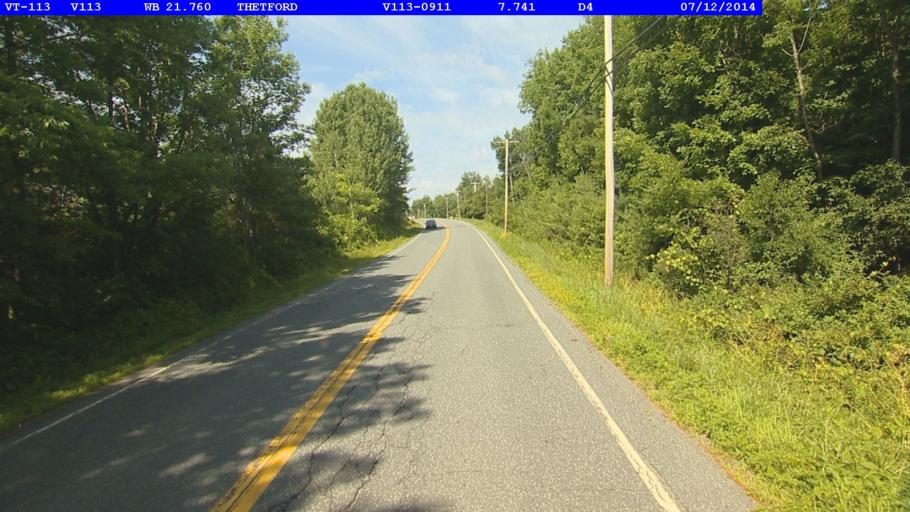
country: US
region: New Hampshire
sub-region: Grafton County
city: Lyme
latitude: 43.8128
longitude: -72.2029
